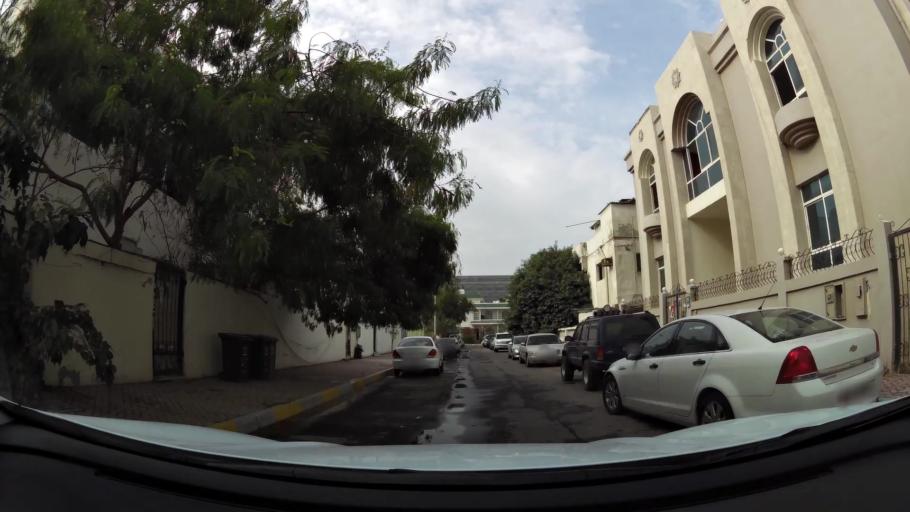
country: AE
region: Abu Dhabi
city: Abu Dhabi
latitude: 24.4511
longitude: 54.3995
